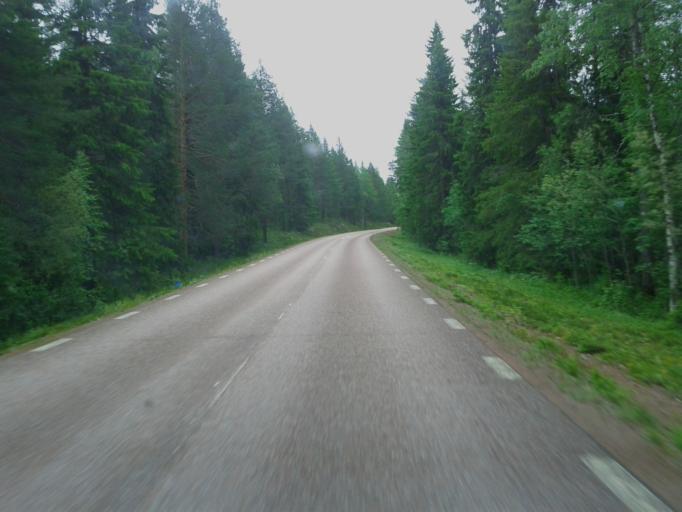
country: NO
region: Hedmark
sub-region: Trysil
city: Innbygda
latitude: 61.8355
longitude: 12.8247
